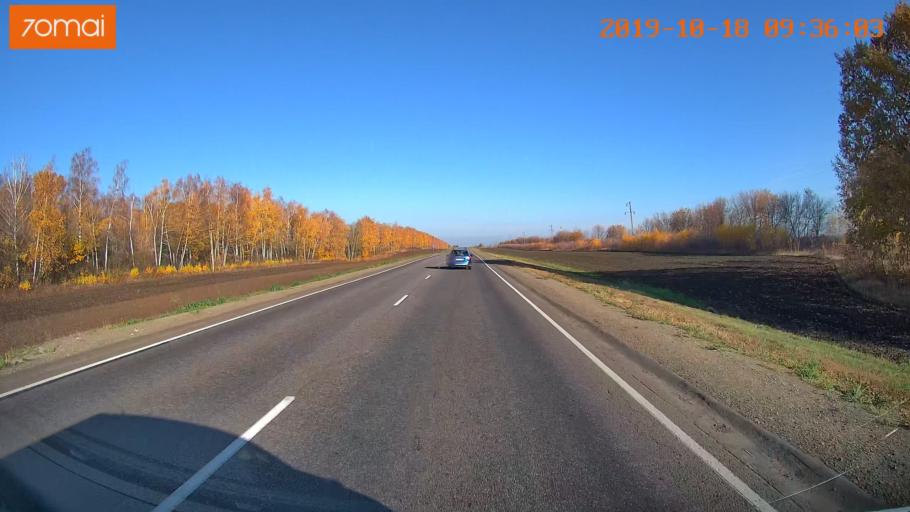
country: RU
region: Tula
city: Yefremov
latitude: 53.2004
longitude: 38.1466
